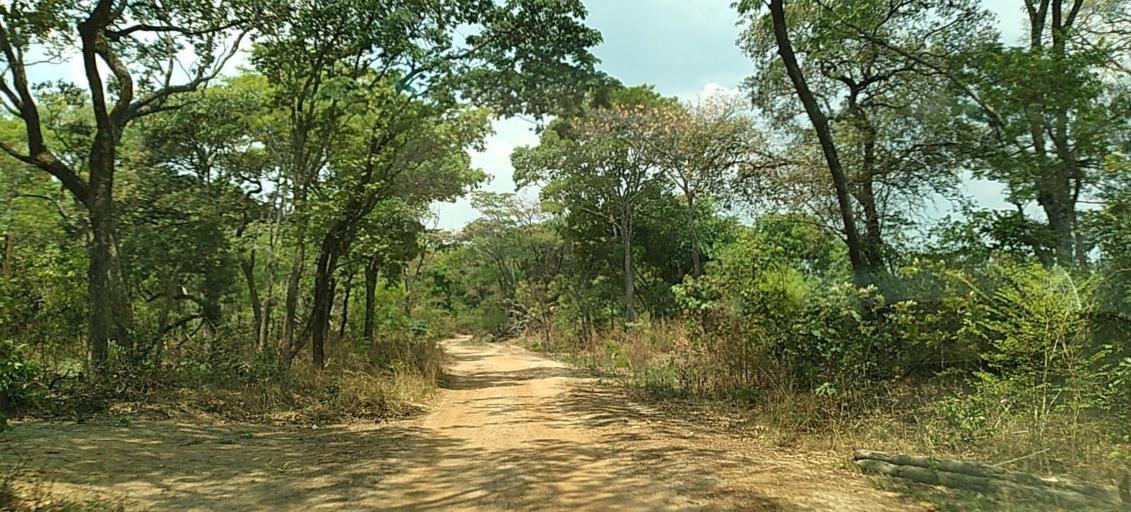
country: ZM
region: Copperbelt
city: Chingola
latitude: -12.7700
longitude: 27.6959
